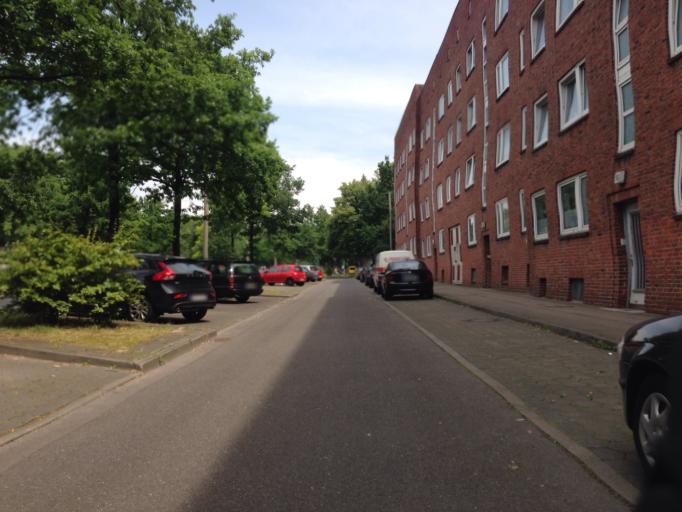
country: DE
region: Hamburg
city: Marienthal
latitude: 53.5836
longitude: 10.0744
